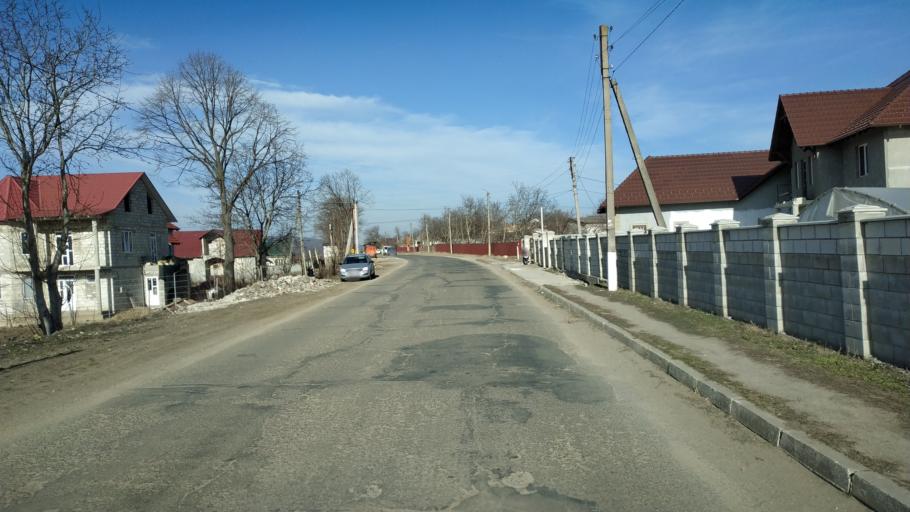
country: MD
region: Chisinau
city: Vatra
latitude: 47.0198
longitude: 28.6490
